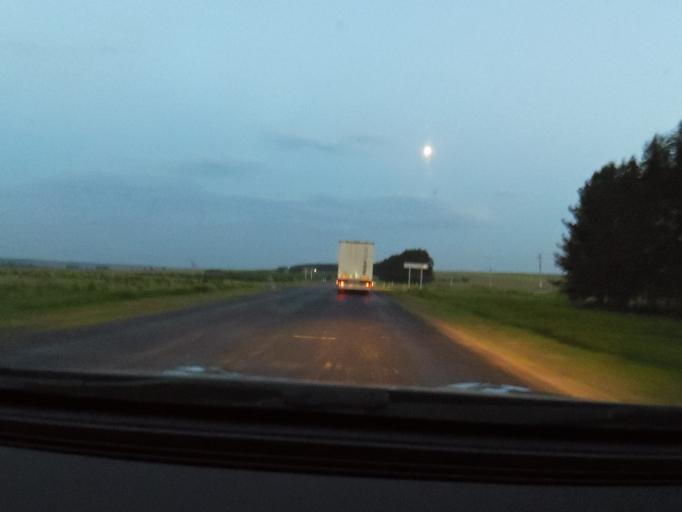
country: RU
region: Bashkortostan
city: Duvan
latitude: 56.0631
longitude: 58.1893
